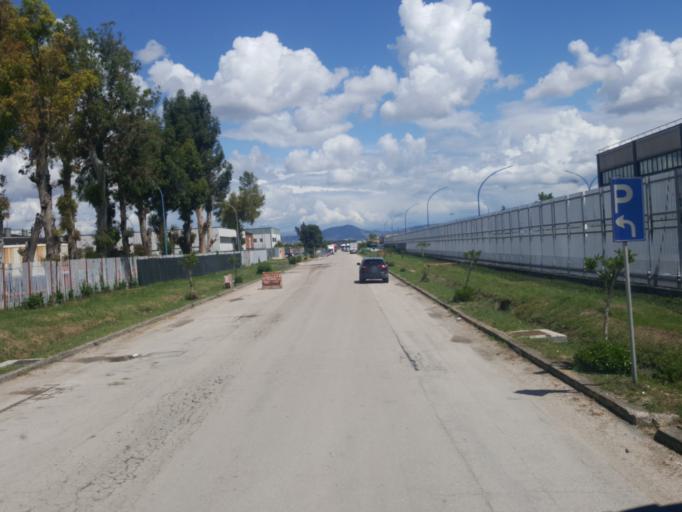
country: IT
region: Campania
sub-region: Provincia di Napoli
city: Pascarola
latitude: 40.9838
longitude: 14.2950
